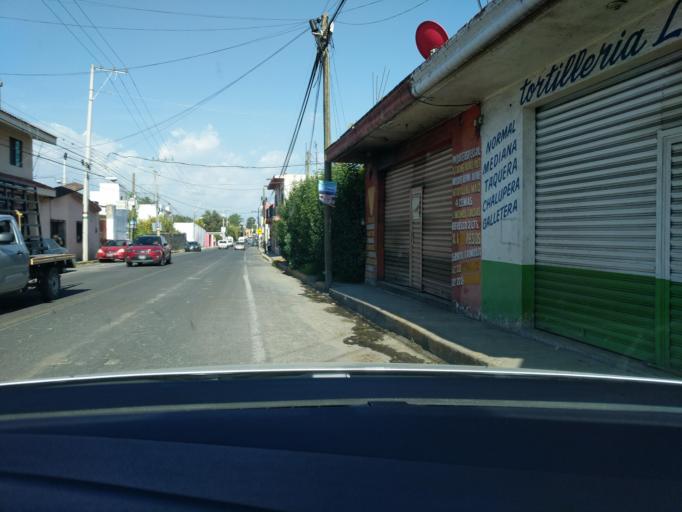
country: MX
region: Puebla
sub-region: San Gregorio Atzompa
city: Chipilo de Francisco Javier Mina
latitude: 19.0066
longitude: -98.3297
